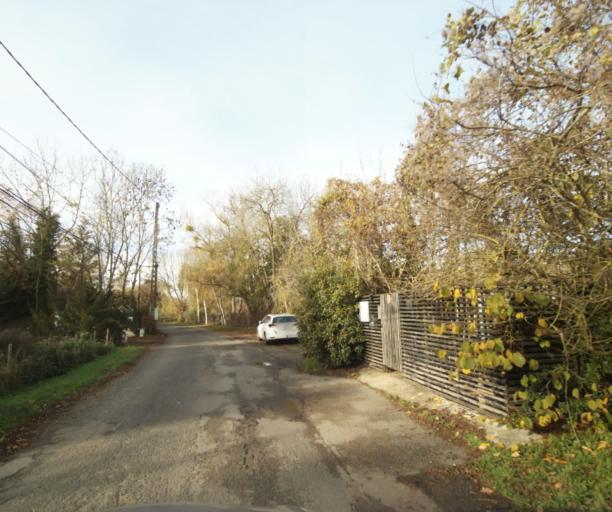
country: FR
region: Ile-de-France
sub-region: Departement du Val-d'Oise
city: Herblay
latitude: 48.9930
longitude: 2.1818
